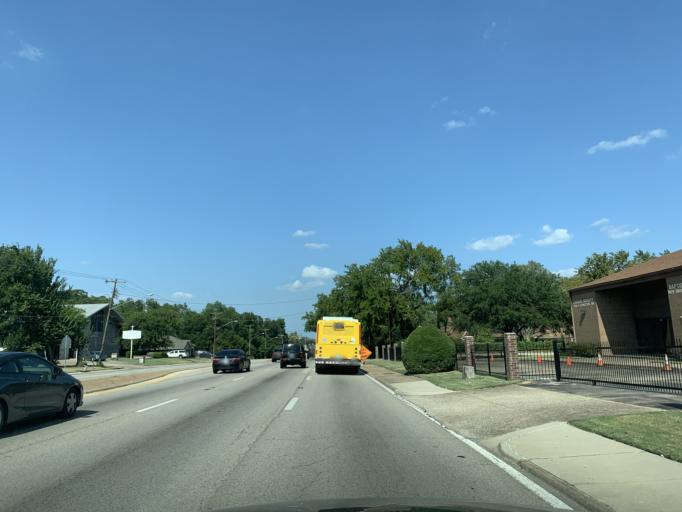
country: US
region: Texas
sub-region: Dallas County
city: Hutchins
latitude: 32.6908
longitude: -96.7795
